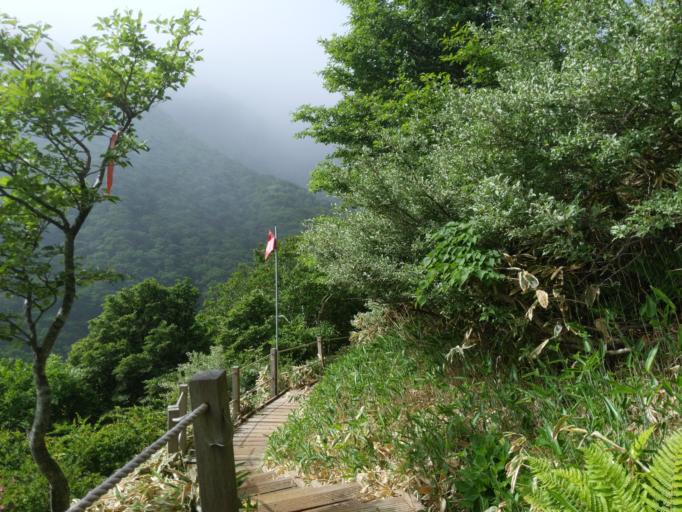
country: KR
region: Jeju-do
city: Seogwipo
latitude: 33.3747
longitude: 126.5300
